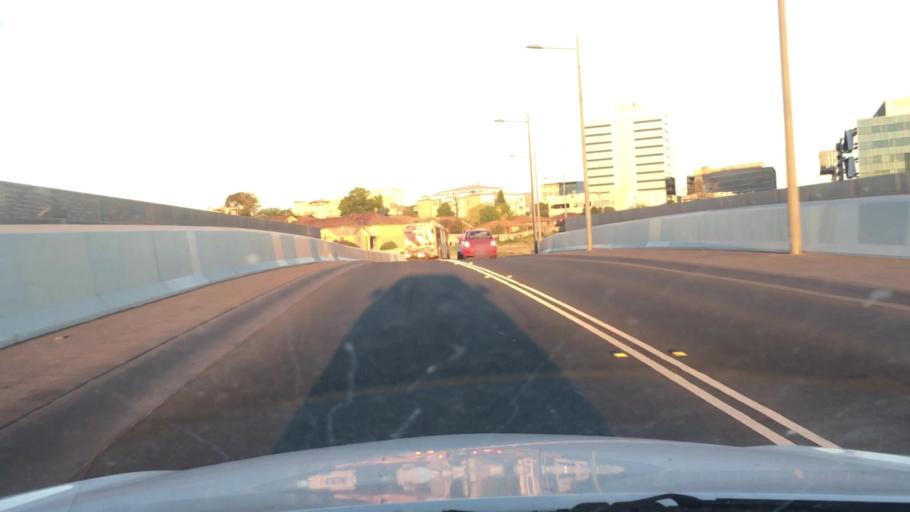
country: AU
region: Victoria
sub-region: Greater Dandenong
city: Dandenong
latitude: -37.9886
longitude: 145.2069
